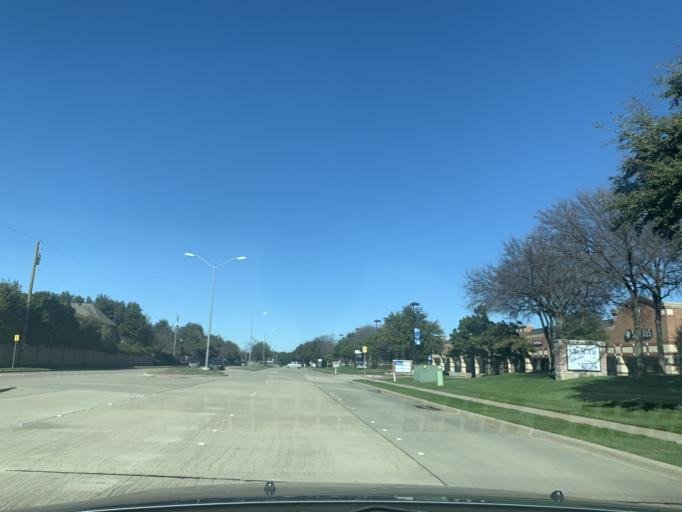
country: US
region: Texas
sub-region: Denton County
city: The Colony
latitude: 33.0478
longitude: -96.8330
